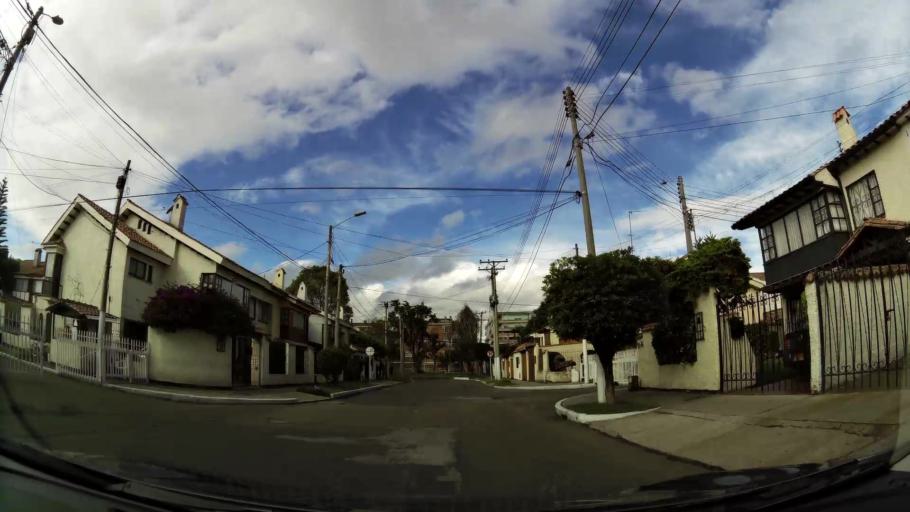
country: CO
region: Bogota D.C.
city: Barrio San Luis
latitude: 4.6924
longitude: -74.0730
